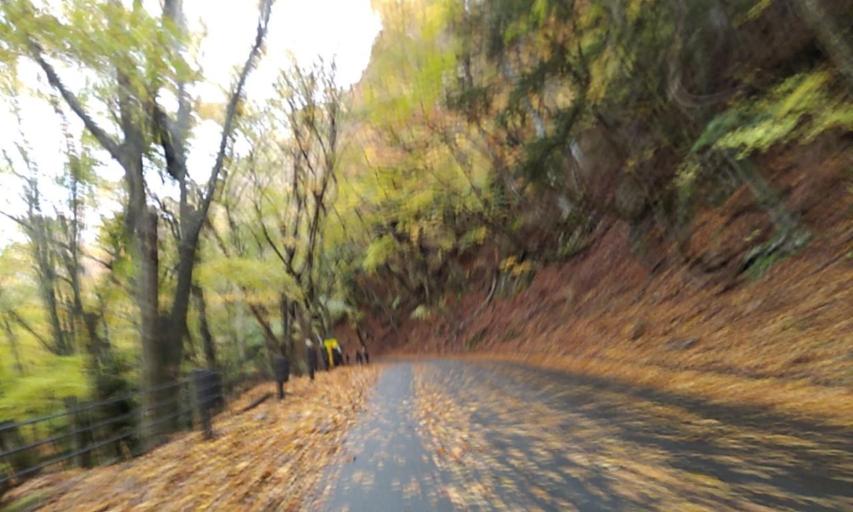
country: JP
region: Yamanashi
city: Fujikawaguchiko
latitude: 35.4509
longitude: 138.5740
